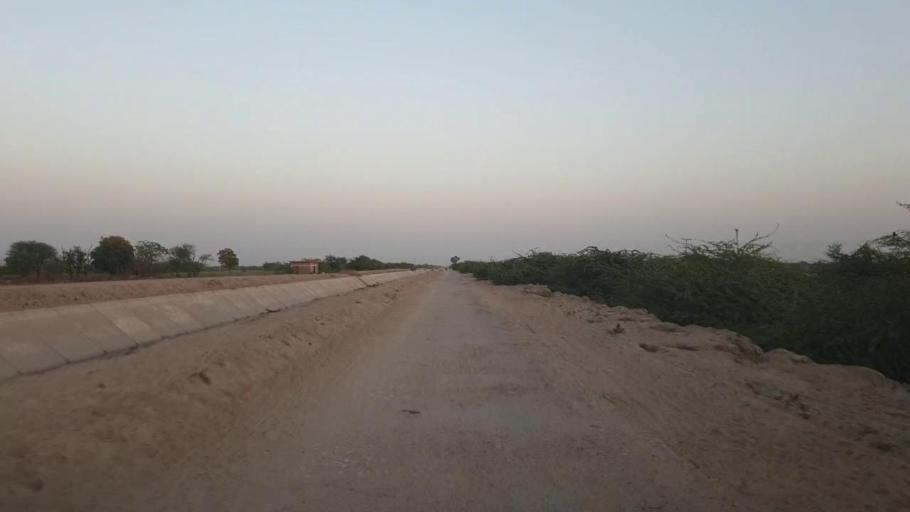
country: PK
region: Sindh
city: Dhoro Naro
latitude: 25.4321
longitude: 69.6496
